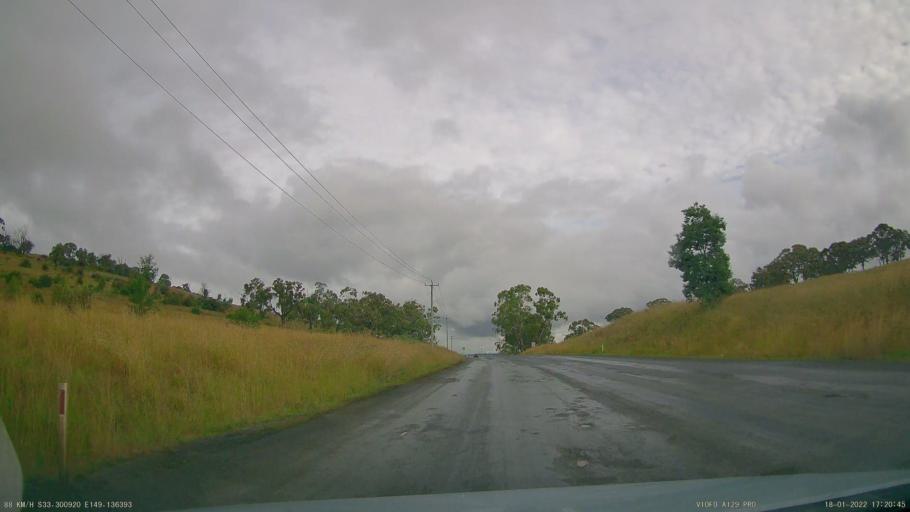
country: AU
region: New South Wales
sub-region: Orange Municipality
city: Orange
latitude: -33.3011
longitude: 149.1365
